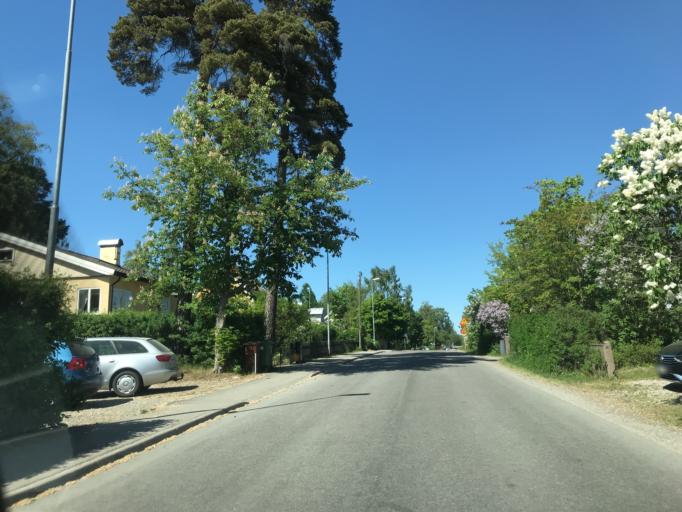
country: SE
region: Stockholm
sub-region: Sollentuna Kommun
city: Sollentuna
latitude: 59.4134
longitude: 17.9730
